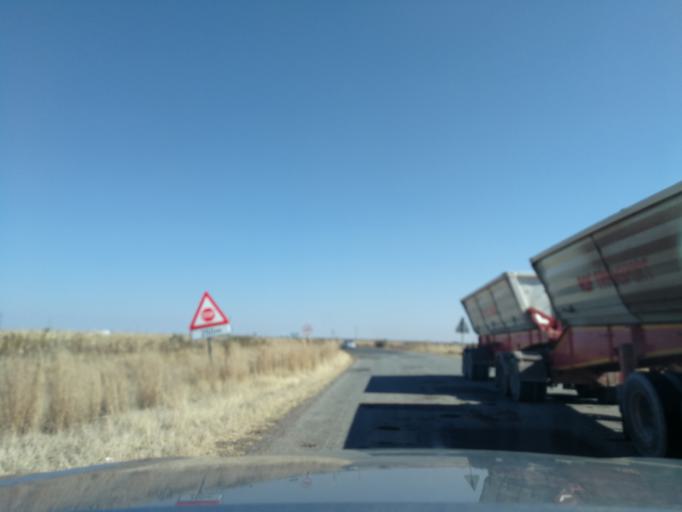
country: ZA
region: North-West
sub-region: Dr Kenneth Kaunda District Municipality
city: Orkney
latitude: -27.0517
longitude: 26.7178
